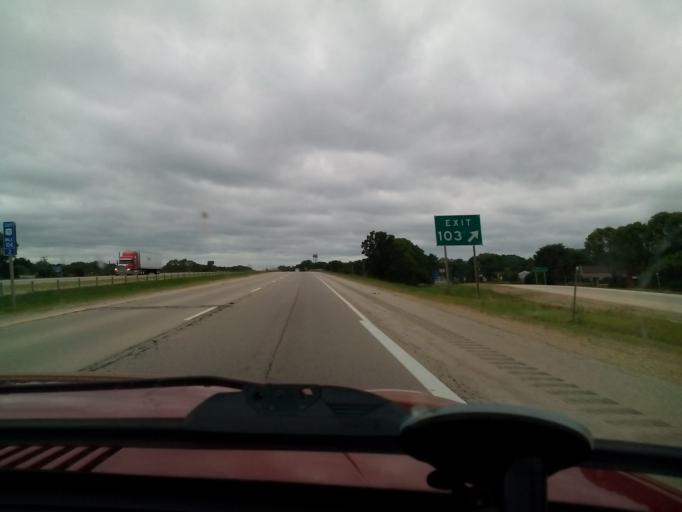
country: US
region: Wisconsin
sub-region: Dane County
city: Sun Prairie
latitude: 43.1983
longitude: -89.2074
